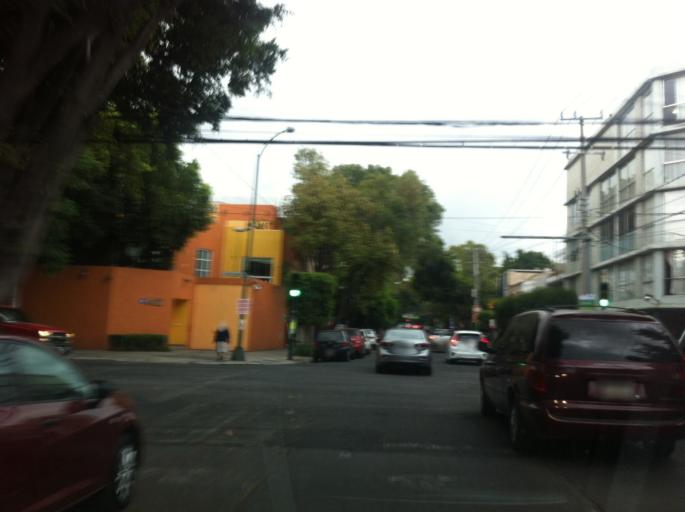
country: MX
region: Mexico City
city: Colonia del Valle
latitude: 19.3754
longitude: -99.1654
